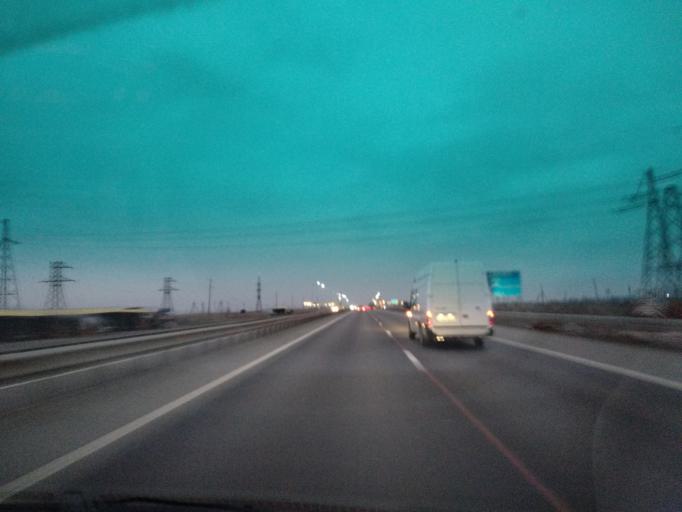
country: RU
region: Adygeya
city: Adygeysk
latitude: 44.8524
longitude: 39.2018
